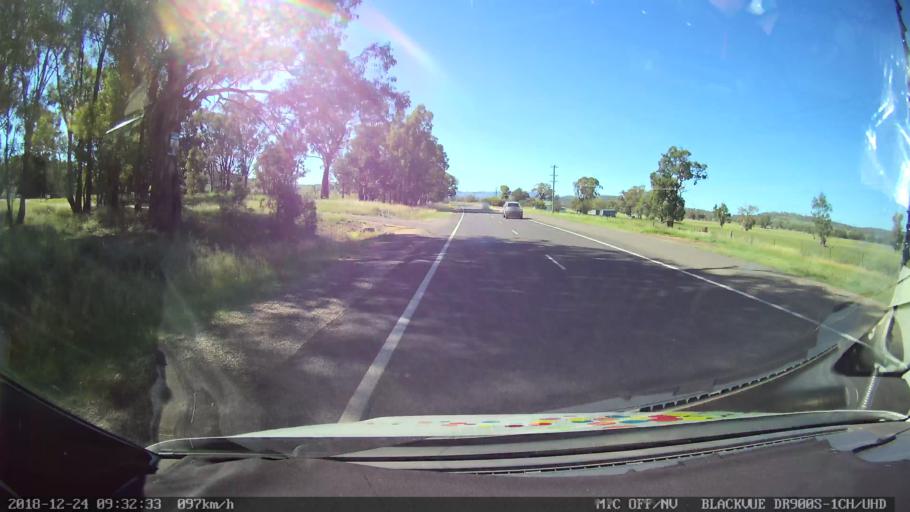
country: AU
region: New South Wales
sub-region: Liverpool Plains
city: Quirindi
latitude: -31.5919
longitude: 150.7032
